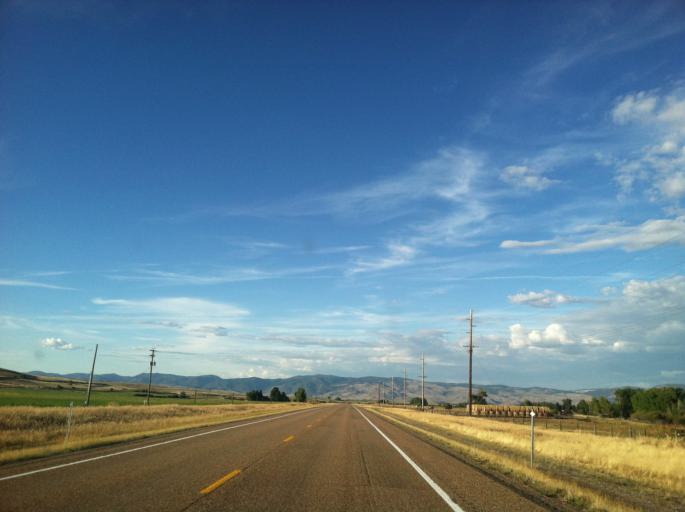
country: US
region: Montana
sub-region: Granite County
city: Philipsburg
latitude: 46.5479
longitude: -113.2188
